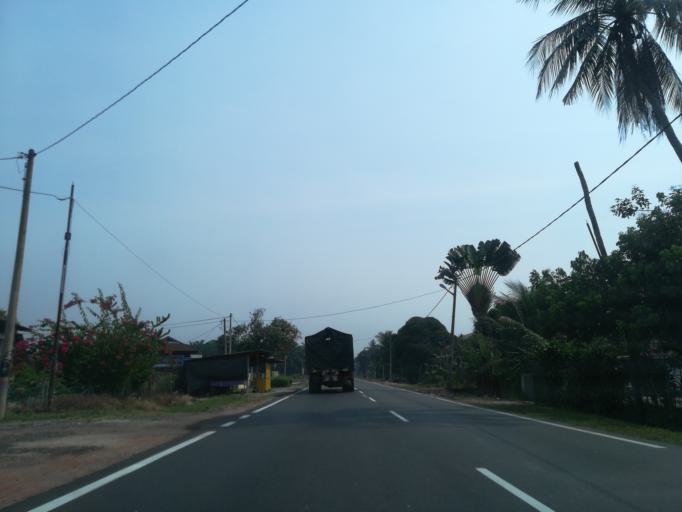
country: MY
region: Penang
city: Tasek Glugor
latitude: 5.4580
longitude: 100.5469
